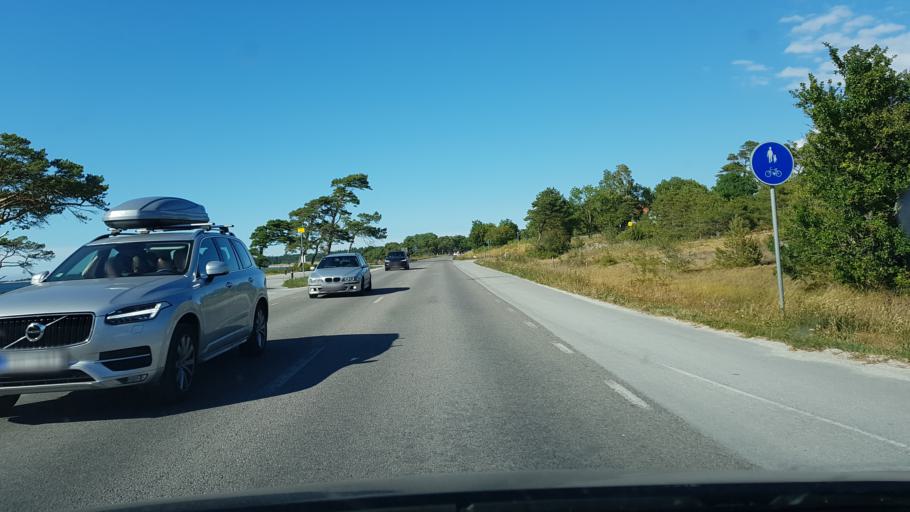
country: SE
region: Gotland
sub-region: Gotland
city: Klintehamn
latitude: 57.4792
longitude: 18.1259
